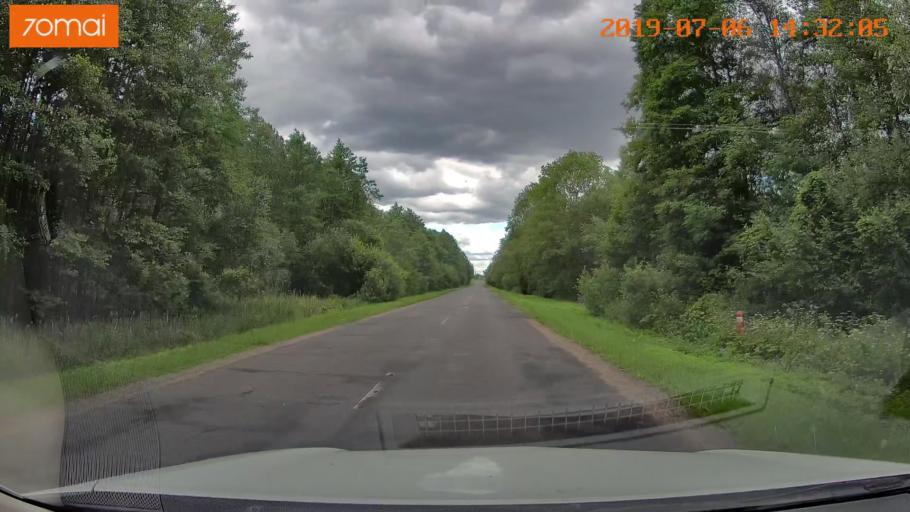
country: BY
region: Minsk
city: Ivyanyets
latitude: 53.9111
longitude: 26.7647
